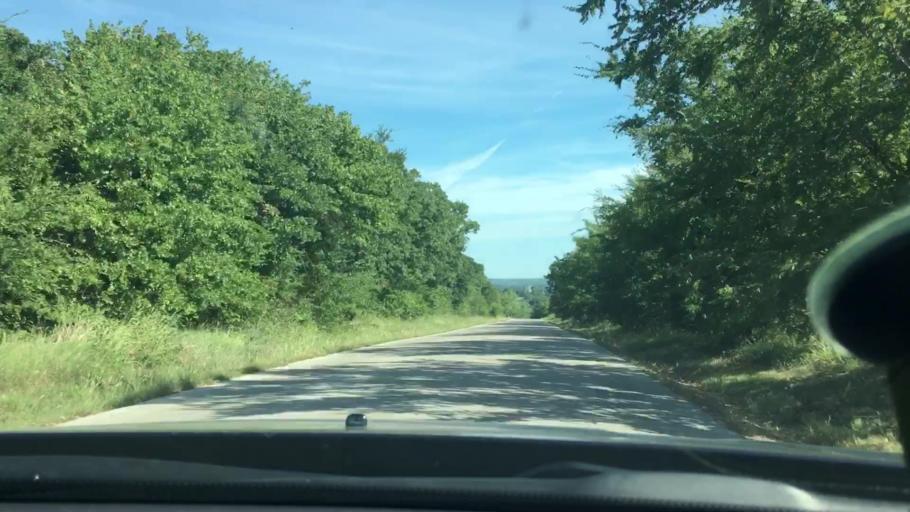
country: US
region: Oklahoma
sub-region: Carter County
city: Lone Grove
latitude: 34.2747
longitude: -97.2824
